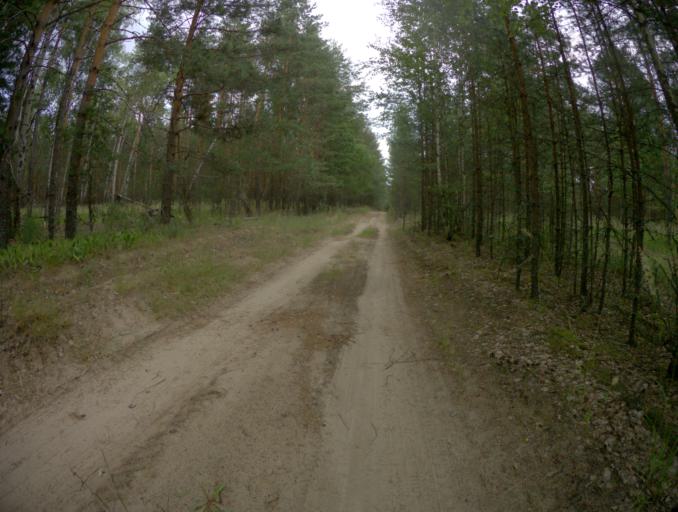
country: RU
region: Nizjnij Novgorod
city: Frolishchi
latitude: 56.3421
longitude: 42.7237
